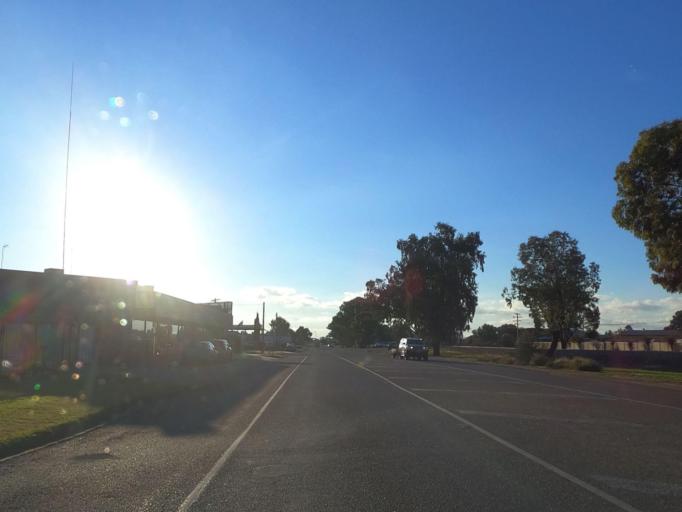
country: AU
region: Victoria
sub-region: Swan Hill
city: Swan Hill
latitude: -35.3314
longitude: 143.5572
